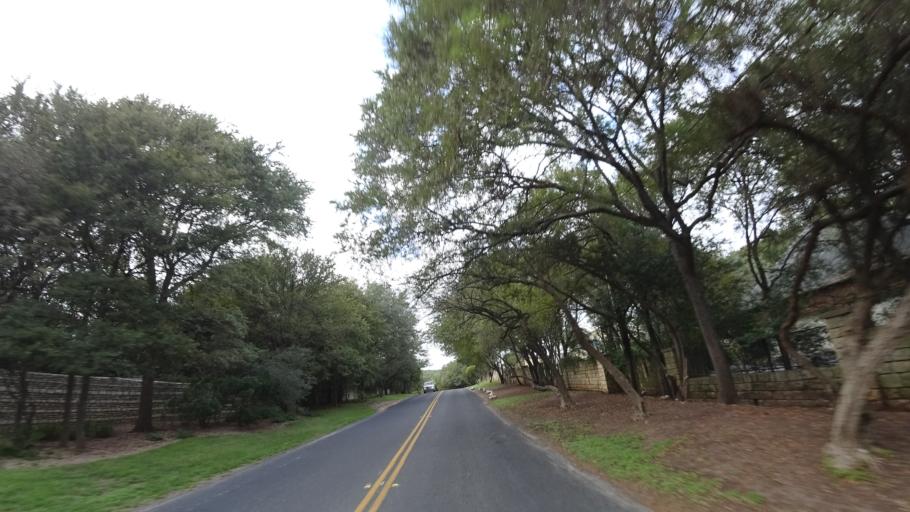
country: US
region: Texas
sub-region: Travis County
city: Rollingwood
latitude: 30.2874
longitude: -97.7895
